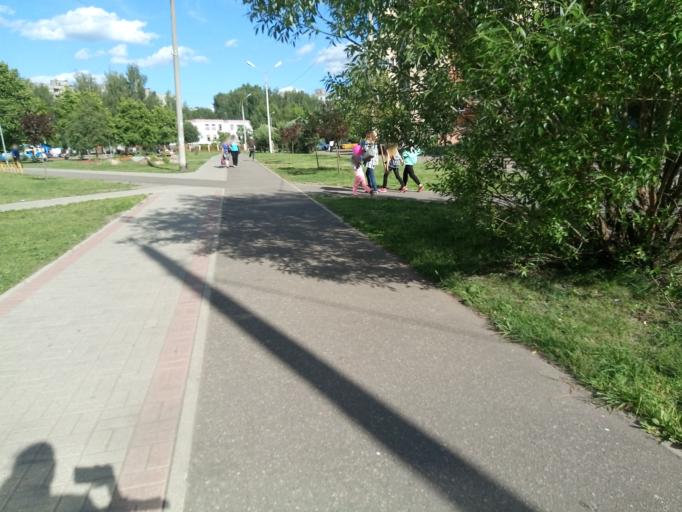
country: RU
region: Jaroslavl
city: Yaroslavl
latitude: 57.6556
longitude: 39.9524
